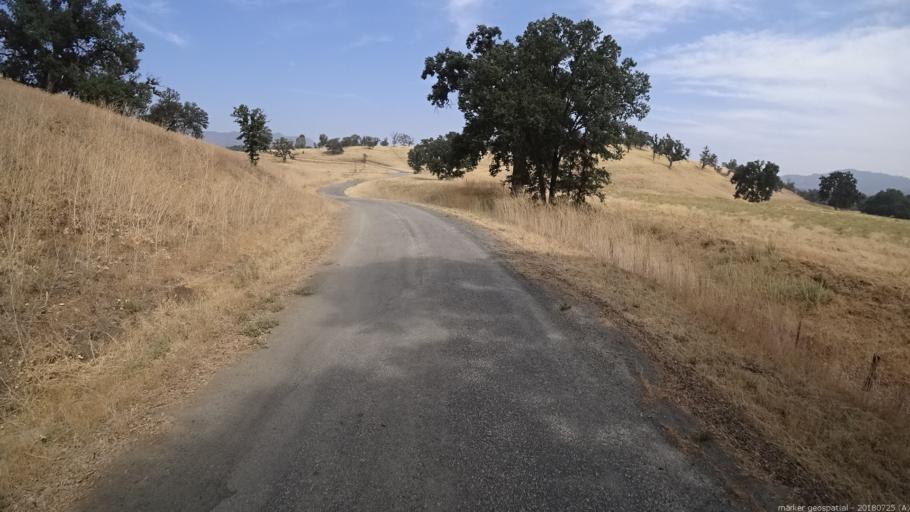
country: US
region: California
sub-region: Fresno County
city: Coalinga
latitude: 36.1833
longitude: -120.6934
